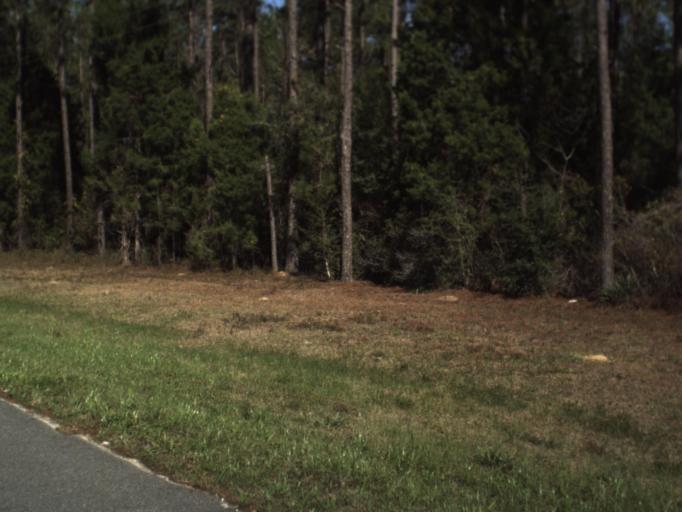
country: US
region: Florida
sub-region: Calhoun County
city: Blountstown
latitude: 30.3171
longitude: -85.1278
